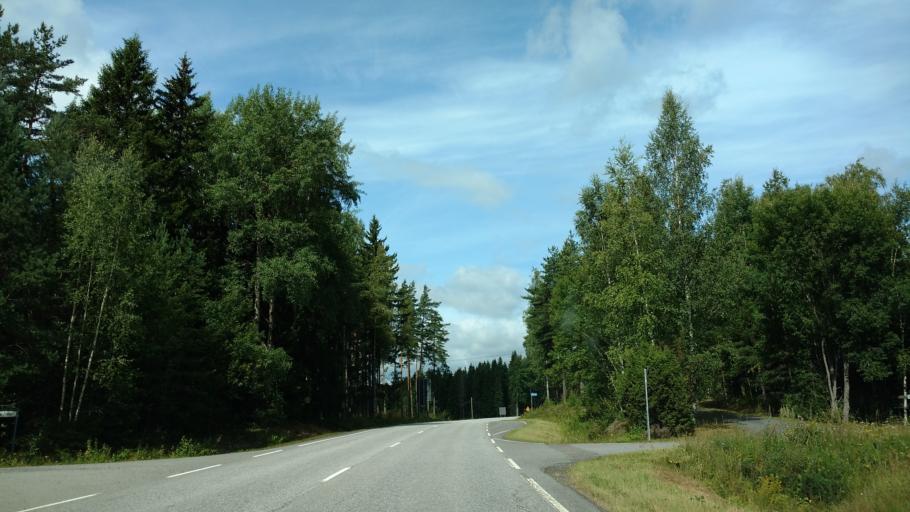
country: FI
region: Varsinais-Suomi
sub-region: Salo
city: Saerkisalo
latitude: 60.1748
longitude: 22.9574
